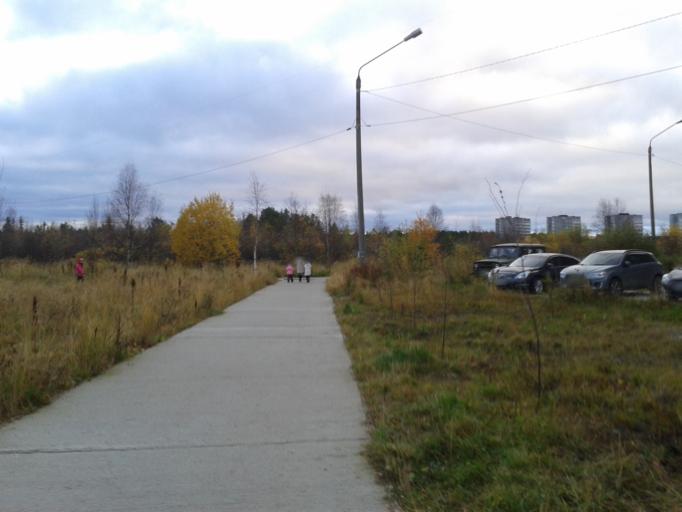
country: RU
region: Murmansk
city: Polyarnyye Zori
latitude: 67.3641
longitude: 32.4854
